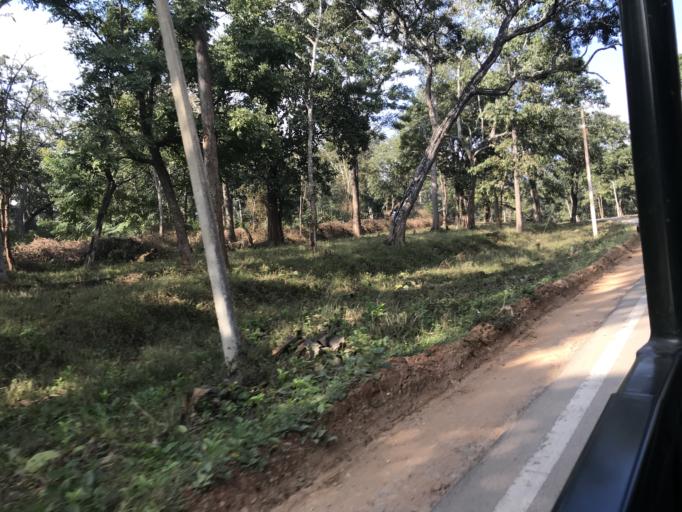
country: IN
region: Karnataka
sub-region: Mysore
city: Heggadadevankote
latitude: 11.9431
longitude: 76.2134
